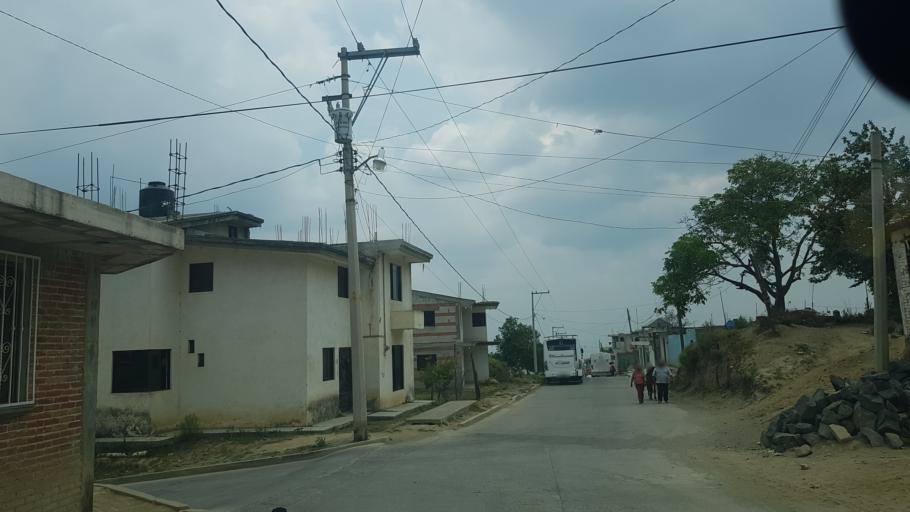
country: MX
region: Puebla
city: Domingo Arenas
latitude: 19.1529
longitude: -98.5037
